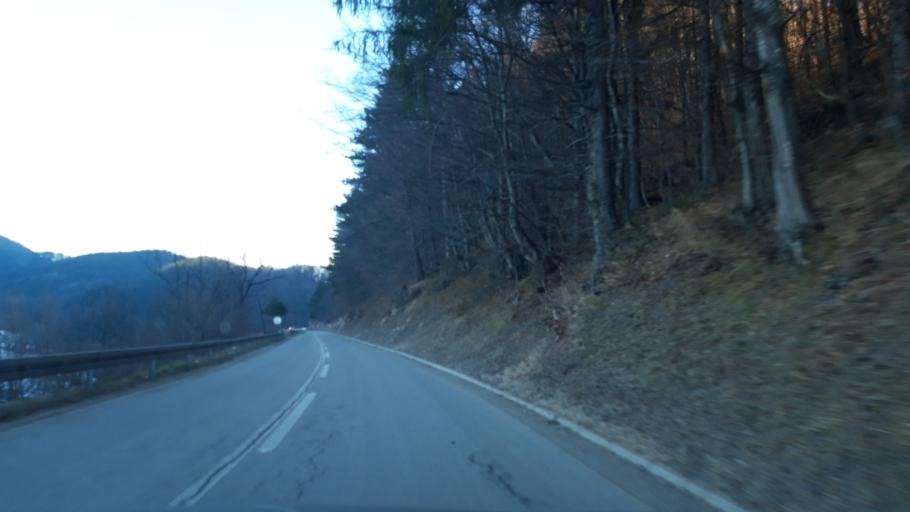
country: BA
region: Republika Srpska
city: Vlasenica
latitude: 44.1691
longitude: 18.9492
